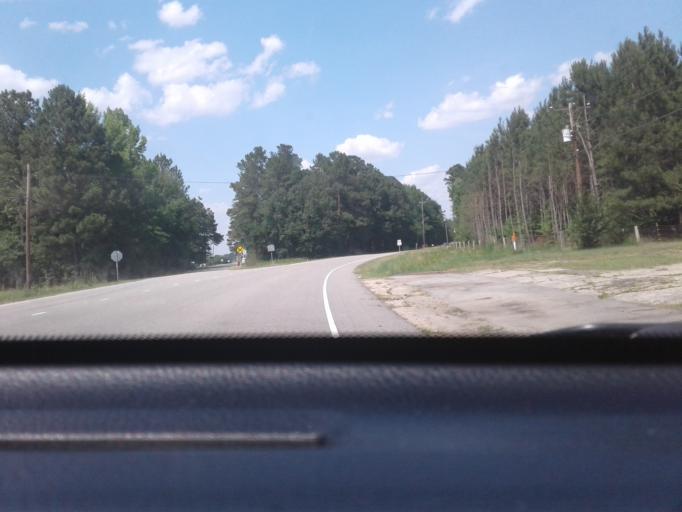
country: US
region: North Carolina
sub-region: Cumberland County
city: Eastover
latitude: 35.1723
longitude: -78.7221
